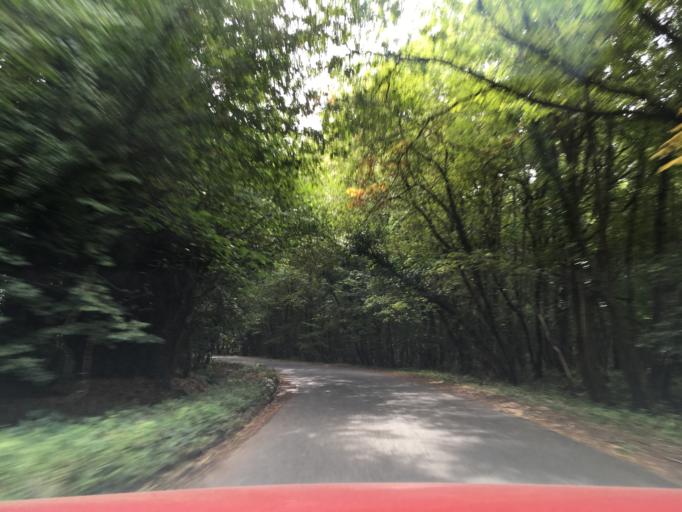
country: GB
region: England
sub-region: South Gloucestershire
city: Charfield
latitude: 51.6537
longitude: -2.4220
